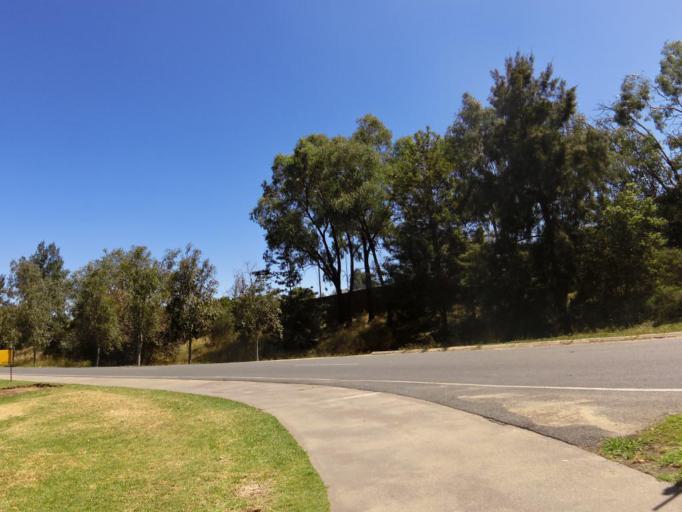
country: AU
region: Victoria
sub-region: Wodonga
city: Wodonga
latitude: -36.1117
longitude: 146.8923
